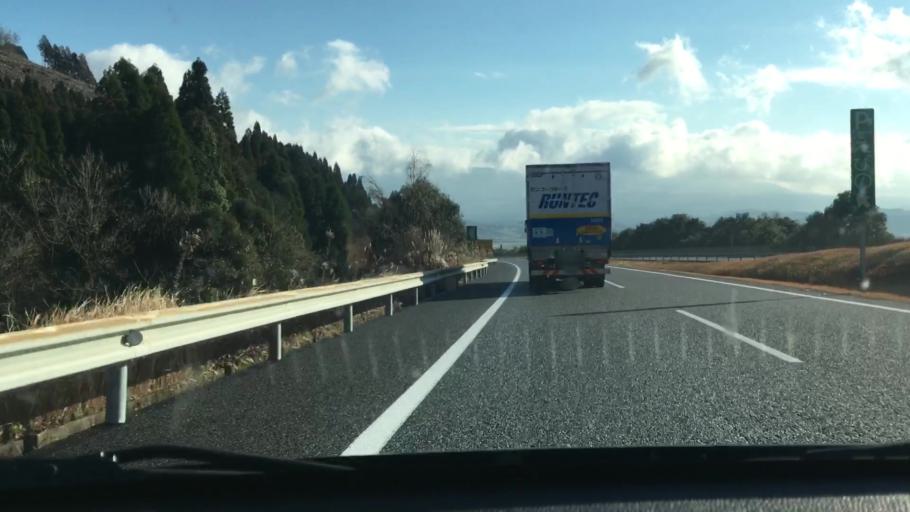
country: JP
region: Kumamoto
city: Hitoyoshi
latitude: 32.0749
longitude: 130.7931
